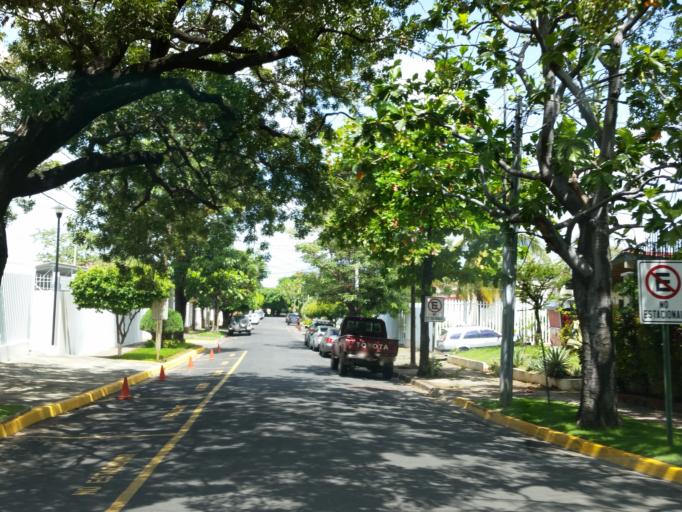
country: NI
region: Managua
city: Managua
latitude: 12.1184
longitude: -86.2580
